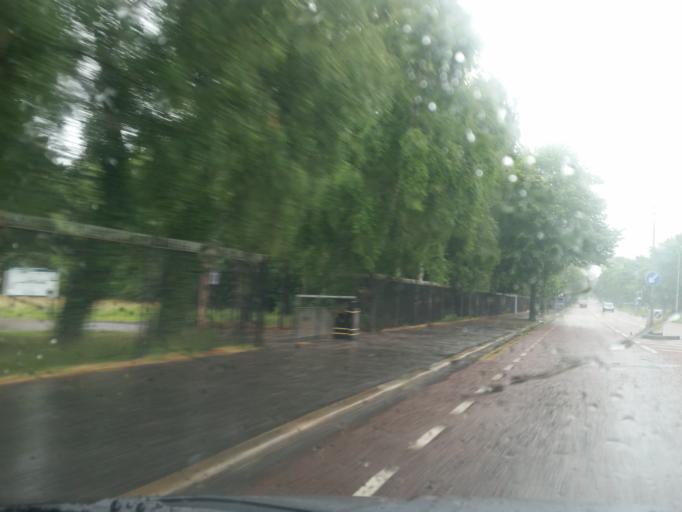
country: GB
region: Northern Ireland
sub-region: Castlereagh District
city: Castlereagh
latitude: 54.6090
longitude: -5.8678
